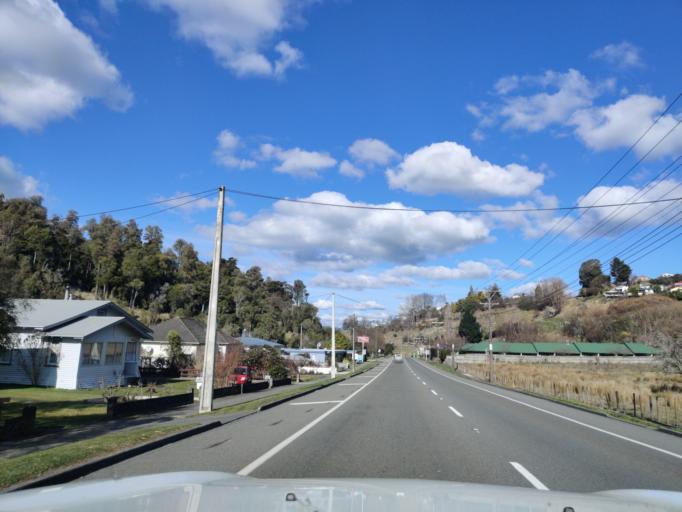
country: NZ
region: Manawatu-Wanganui
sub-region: Ruapehu District
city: Waiouru
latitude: -39.6711
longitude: 175.7914
